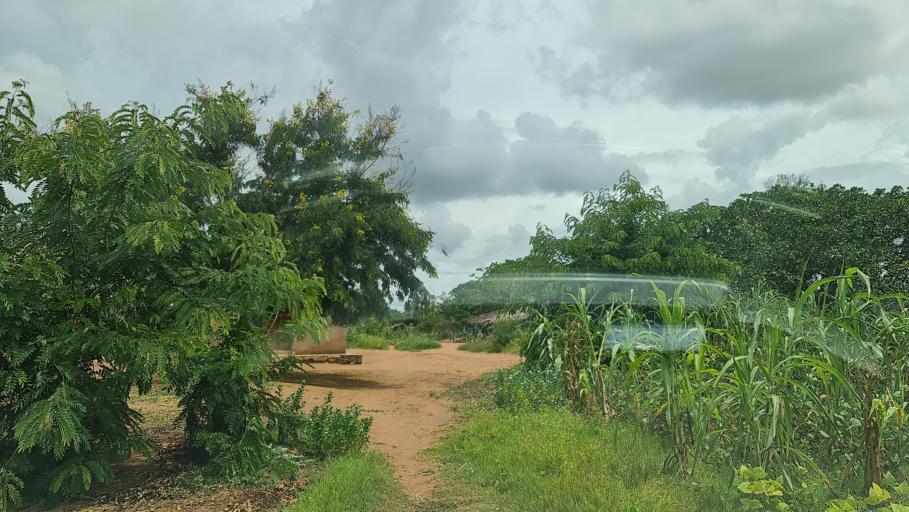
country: MZ
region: Nampula
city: Nacala
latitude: -14.7829
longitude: 39.9959
